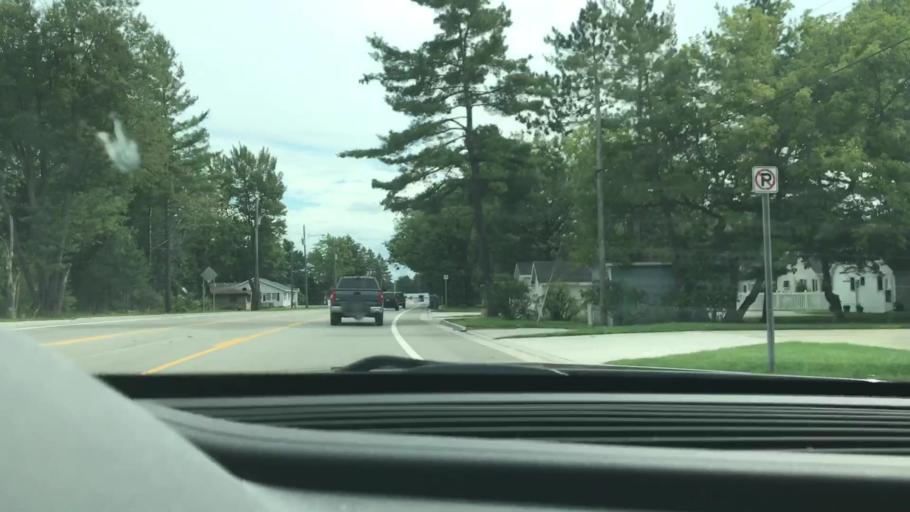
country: US
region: Michigan
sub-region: Missaukee County
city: Lake City
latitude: 44.3241
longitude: -85.2119
